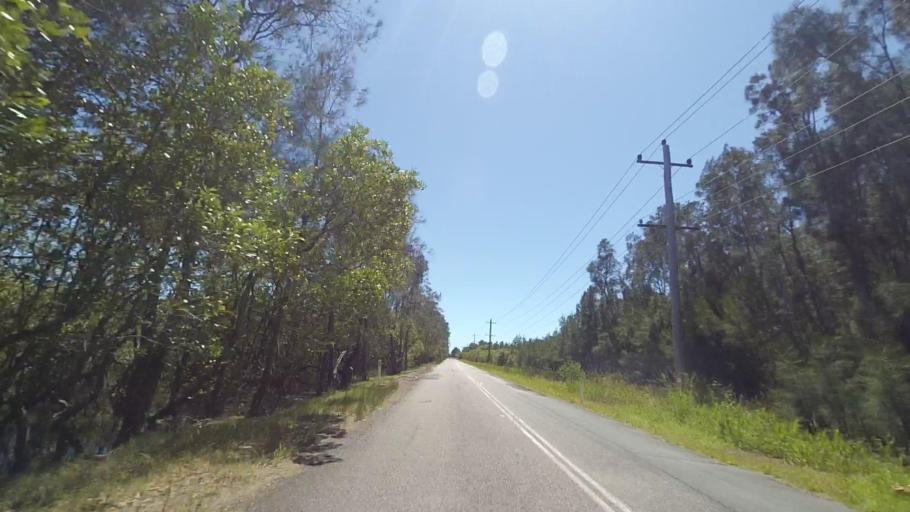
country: AU
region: New South Wales
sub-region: Port Stephens Shire
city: Medowie
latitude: -32.7864
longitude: 151.9363
